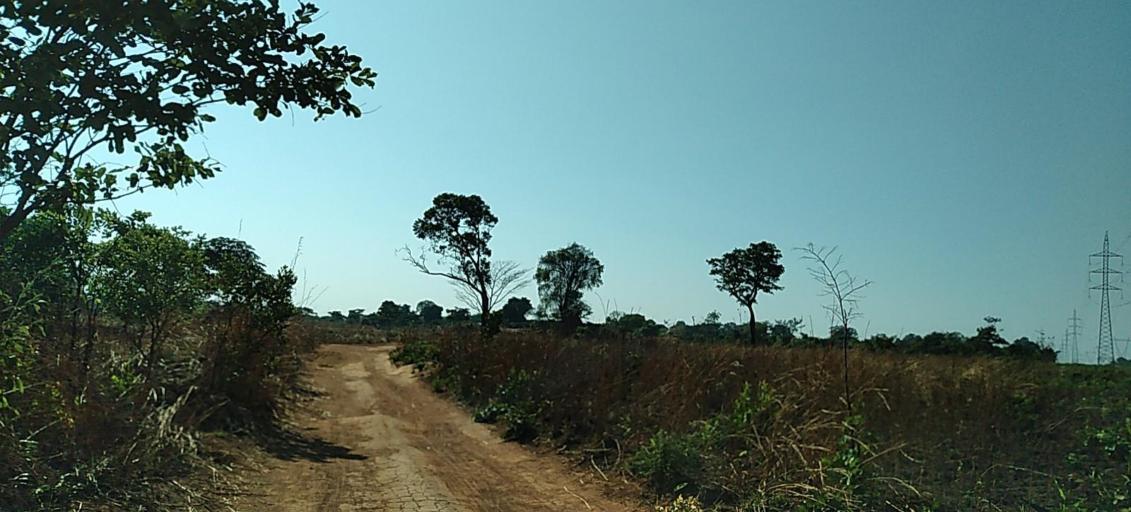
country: ZM
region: Copperbelt
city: Chililabombwe
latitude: -12.3684
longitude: 27.8989
